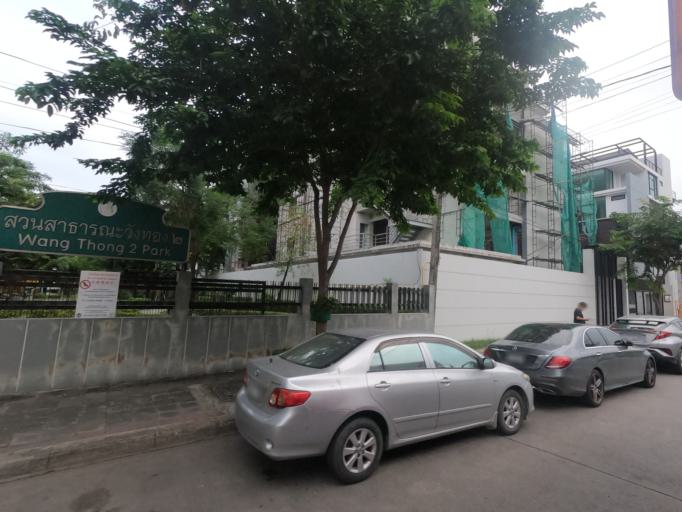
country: TH
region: Bangkok
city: Wang Thonglang
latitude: 13.7917
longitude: 100.6085
